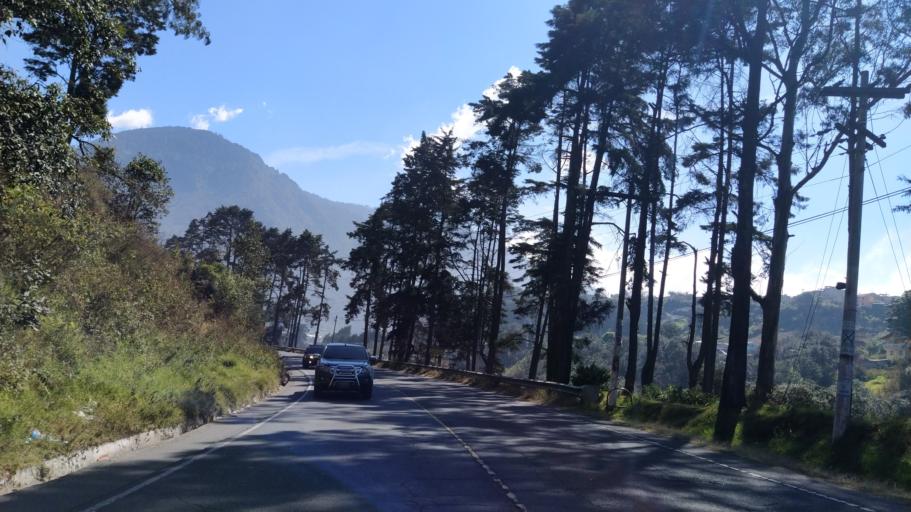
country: GT
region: Quetzaltenango
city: Cantel
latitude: 14.8152
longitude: -91.4531
